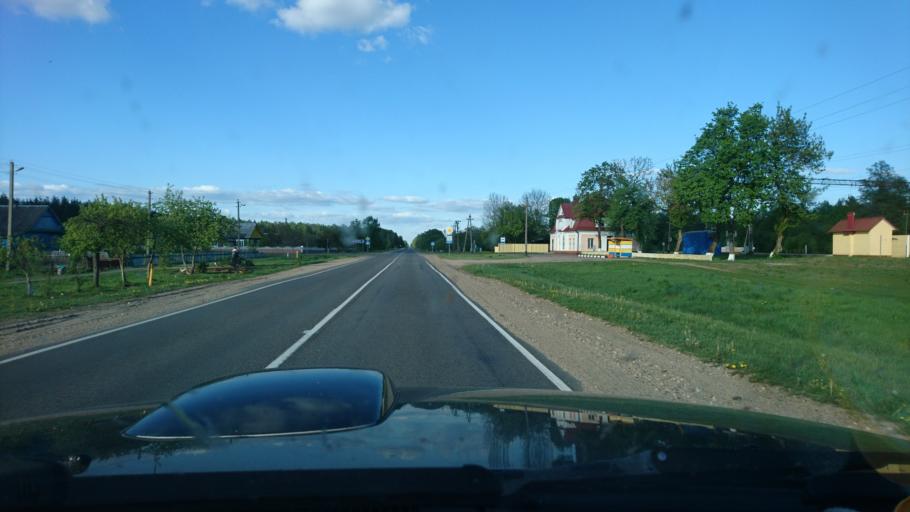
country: BY
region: Brest
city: Nyakhachava
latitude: 52.6510
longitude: 25.2198
